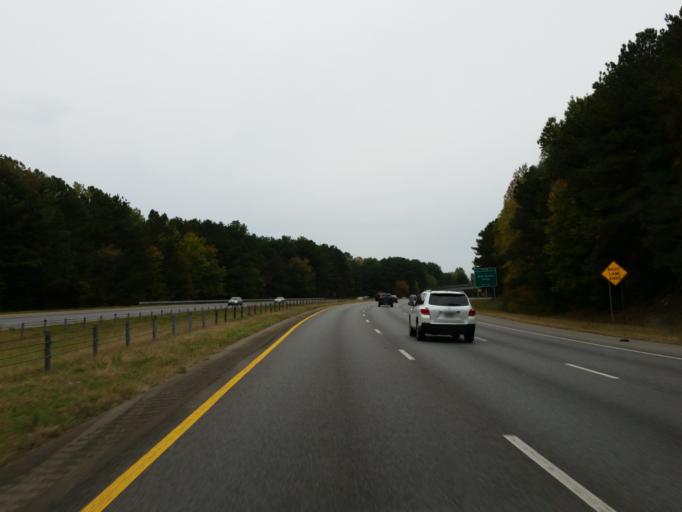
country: US
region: Georgia
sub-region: Cherokee County
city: Holly Springs
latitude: 34.1706
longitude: -84.5130
